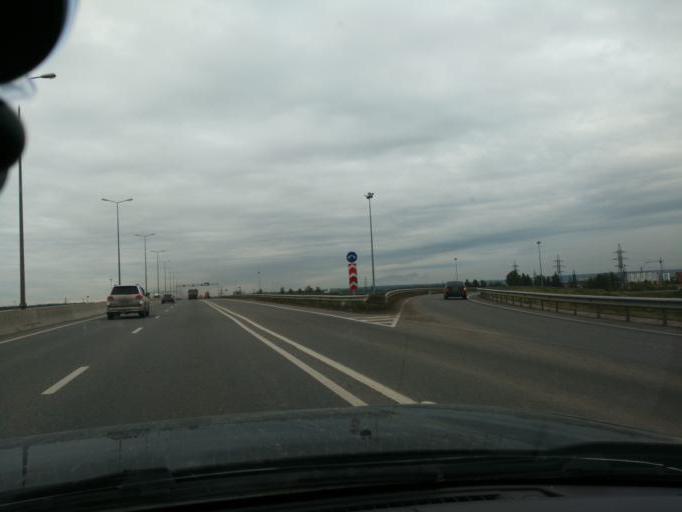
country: RU
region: Perm
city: Froly
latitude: 57.9332
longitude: 56.2621
